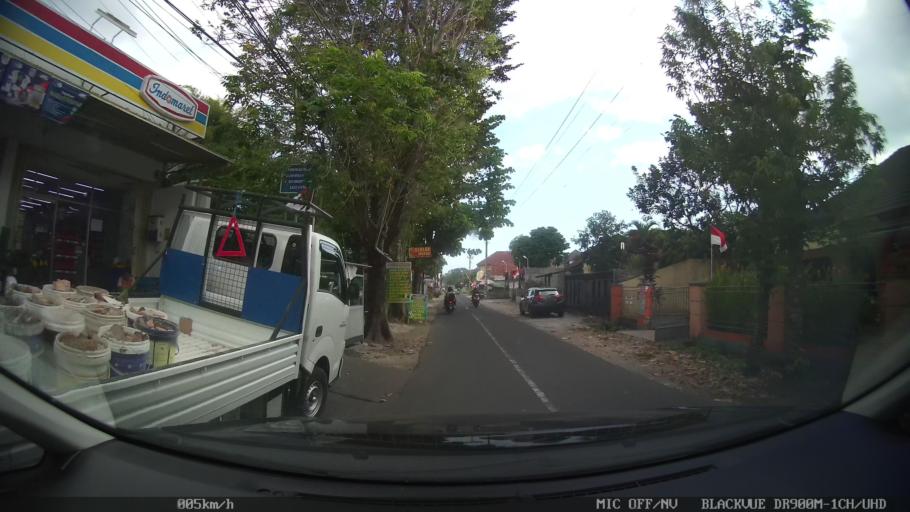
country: ID
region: Daerah Istimewa Yogyakarta
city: Yogyakarta
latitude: -7.7841
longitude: 110.3419
